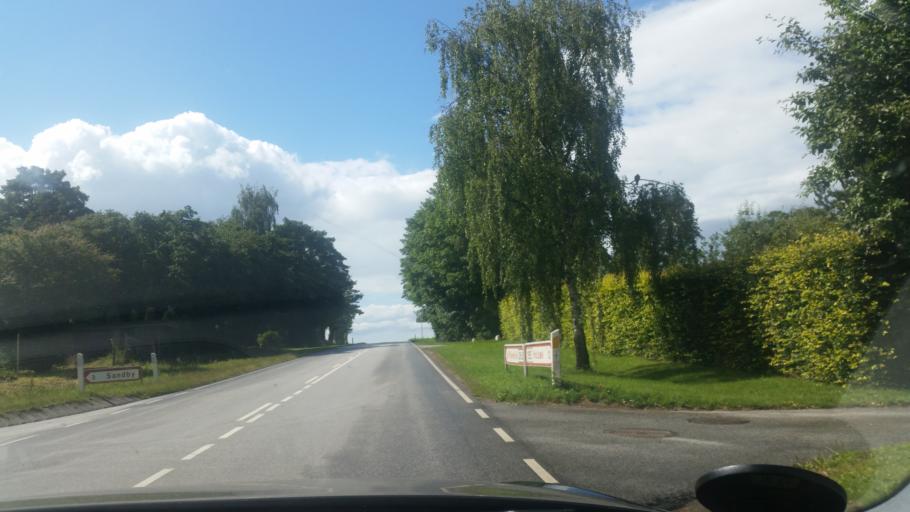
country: DK
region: Zealand
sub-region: Holbaek Kommune
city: Svinninge
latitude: 55.7375
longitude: 11.5460
